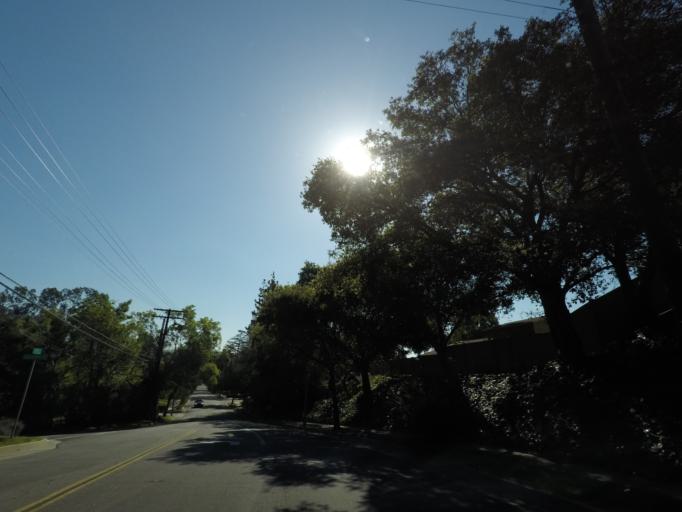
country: US
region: California
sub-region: Los Angeles County
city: La Canada Flintridge
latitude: 34.1714
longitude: -118.1822
